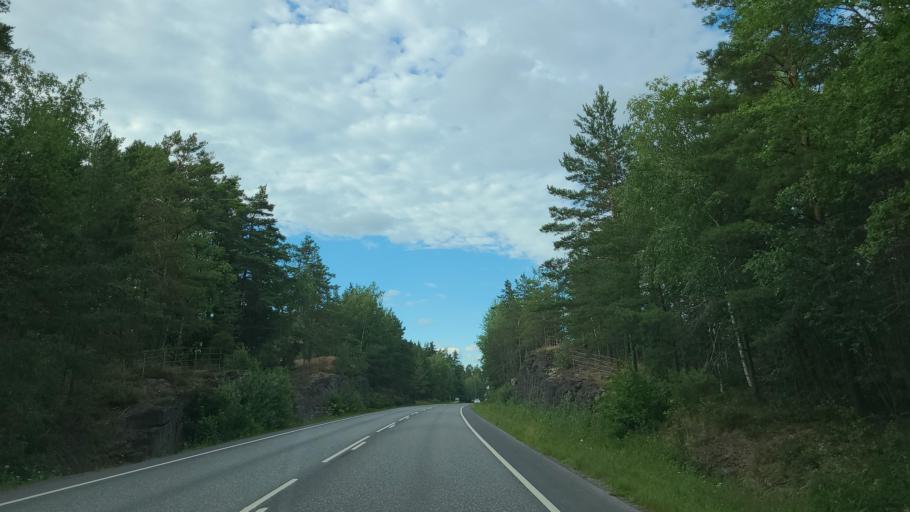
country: FI
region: Varsinais-Suomi
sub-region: Turku
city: Rymaettylae
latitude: 60.4183
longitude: 21.8967
